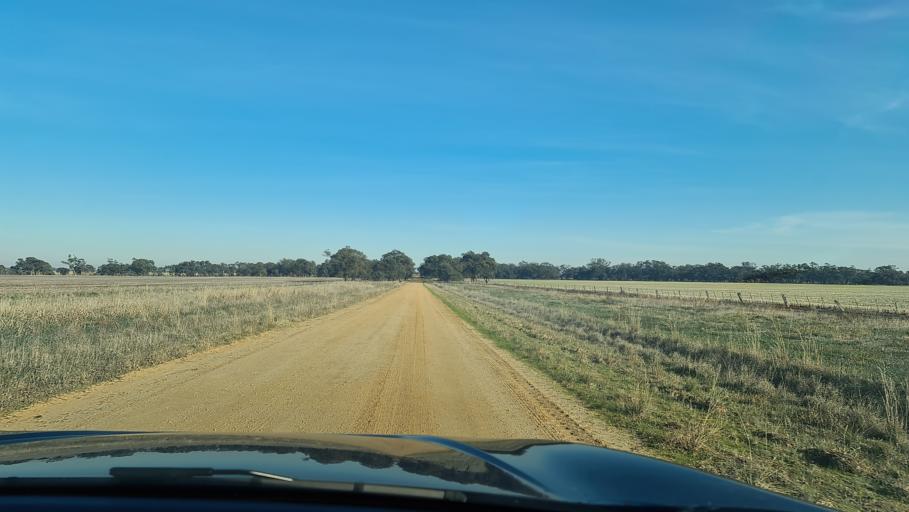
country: AU
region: Victoria
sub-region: Horsham
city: Horsham
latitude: -36.3538
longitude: 142.4033
